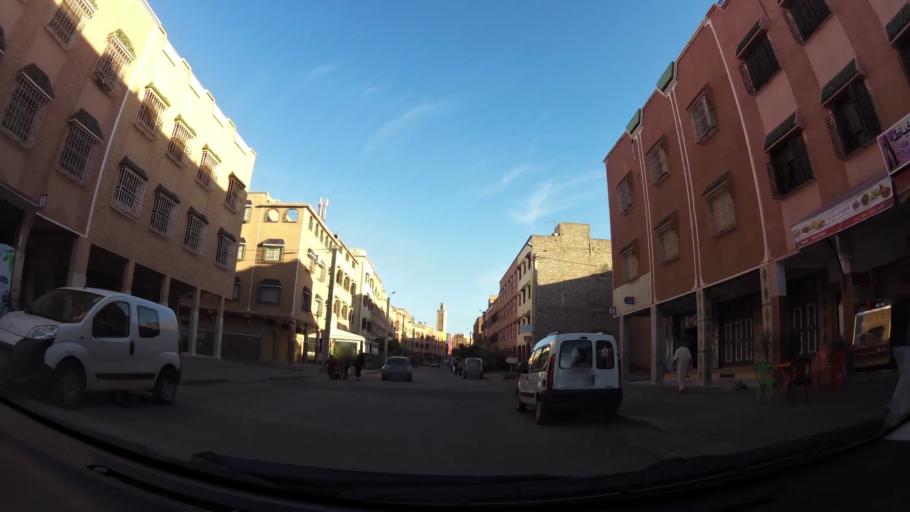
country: MA
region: Marrakech-Tensift-Al Haouz
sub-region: Marrakech
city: Marrakesh
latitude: 31.6194
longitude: -8.0491
